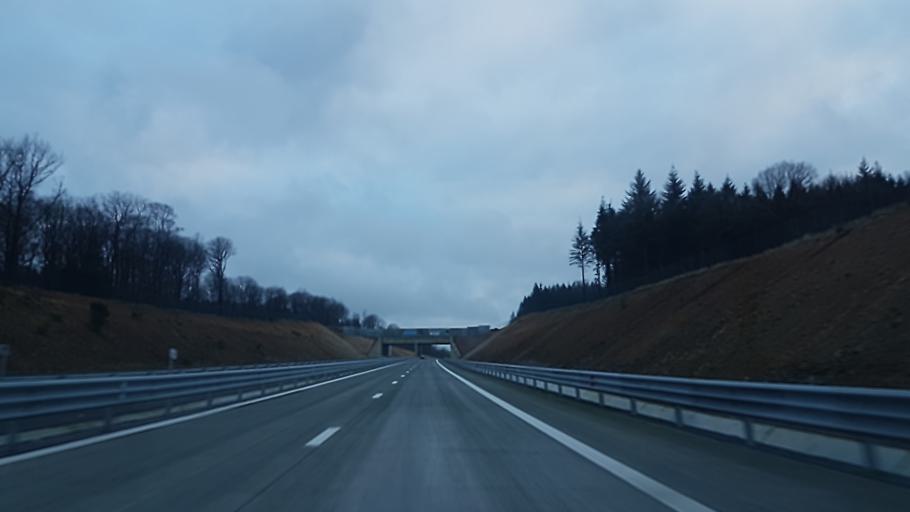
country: BE
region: Wallonia
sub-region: Province de Namur
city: Couvin
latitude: 50.0042
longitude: 4.5394
